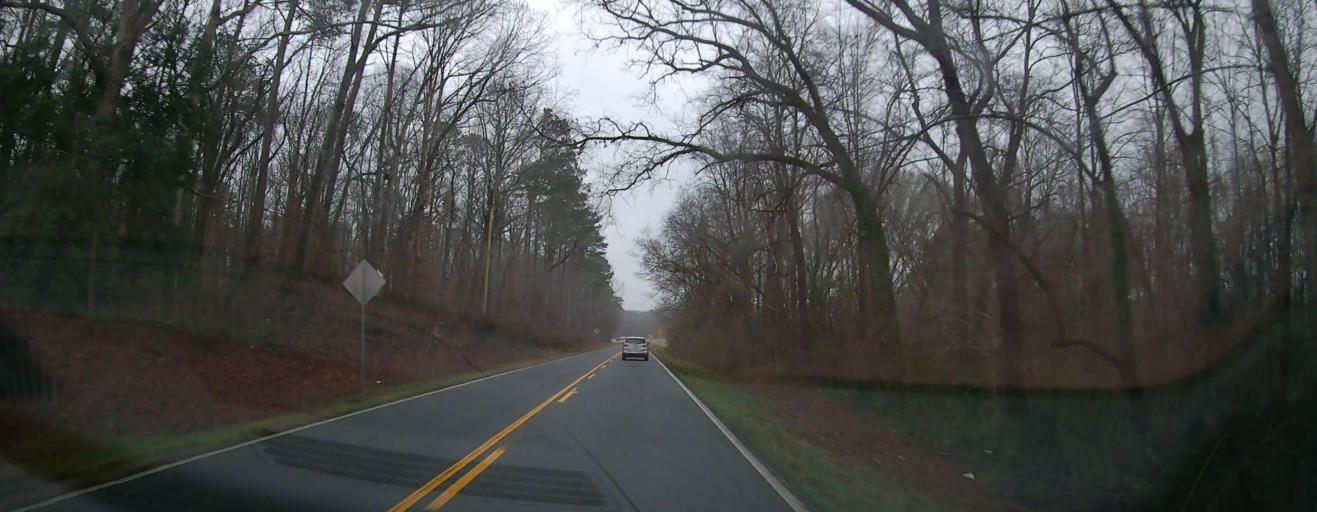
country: US
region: Georgia
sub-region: Spalding County
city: East Griffin
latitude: 33.2278
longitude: -84.2422
